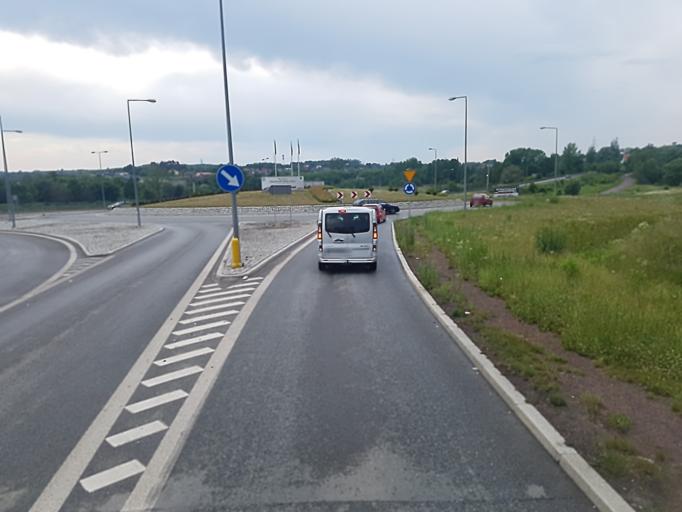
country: PL
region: Silesian Voivodeship
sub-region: Jastrzebie-Zdroj
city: Jastrzebie Zdroj
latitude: 49.9645
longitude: 18.5533
